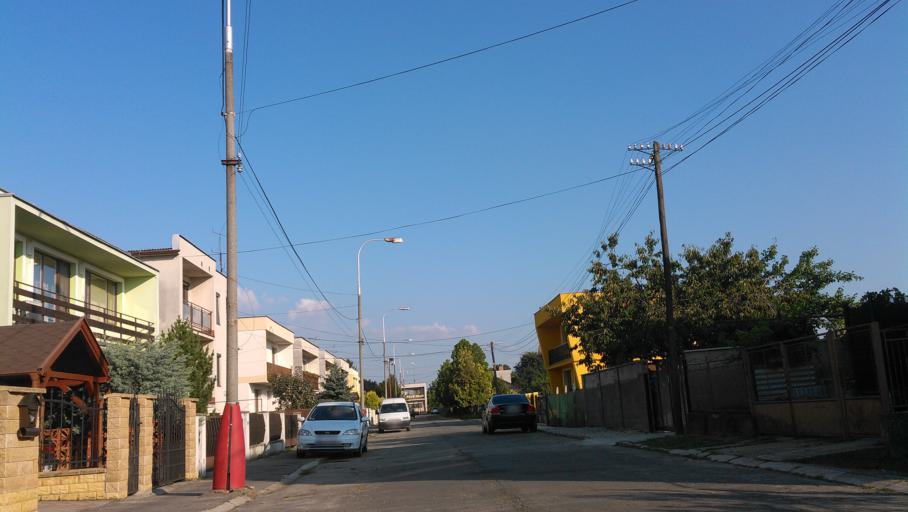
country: SK
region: Nitriansky
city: Kolarovo
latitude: 47.9223
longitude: 17.9893
